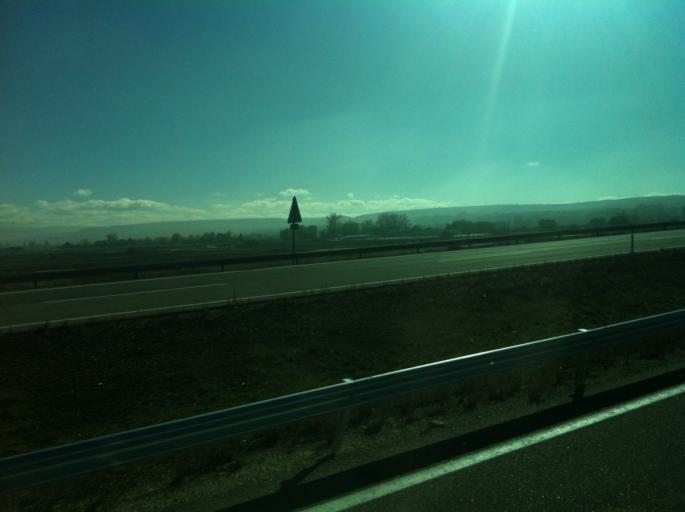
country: ES
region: Castille and Leon
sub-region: Provincia de Burgos
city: Cardenajimeno
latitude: 42.3442
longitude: -3.6057
